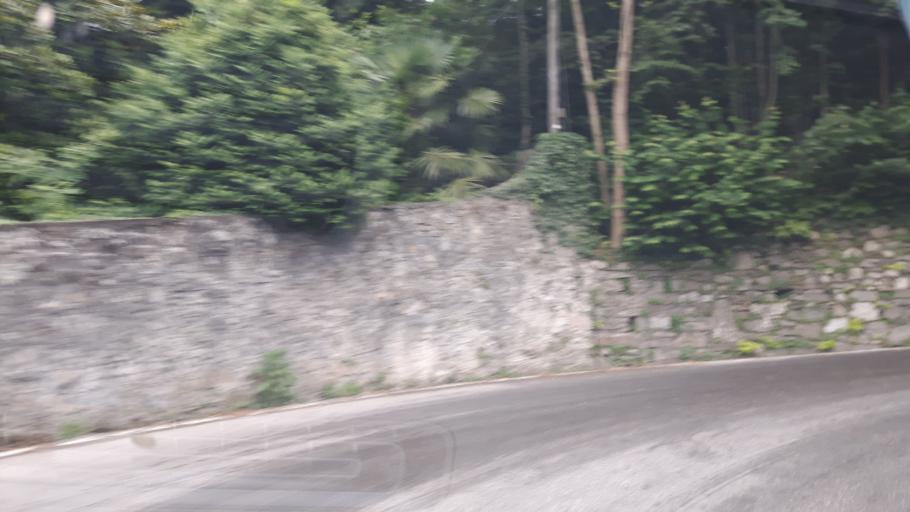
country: IT
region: Piedmont
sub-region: Provincia Verbano-Cusio-Ossola
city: Stresa
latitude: 45.8793
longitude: 8.5425
